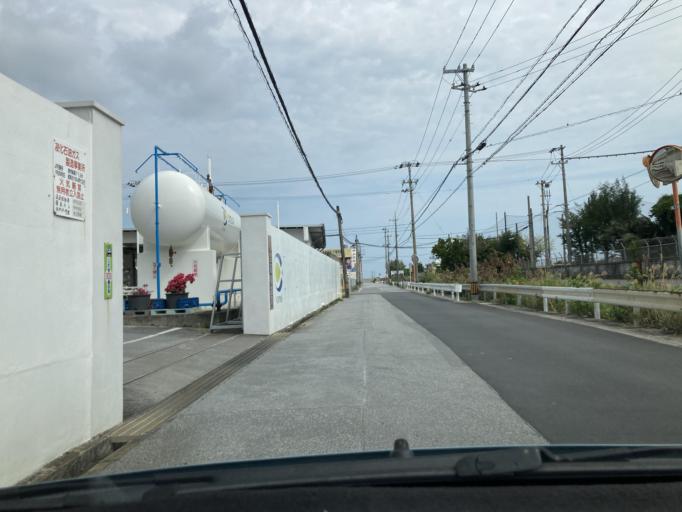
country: JP
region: Okinawa
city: Ginowan
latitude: 26.2708
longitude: 127.7152
